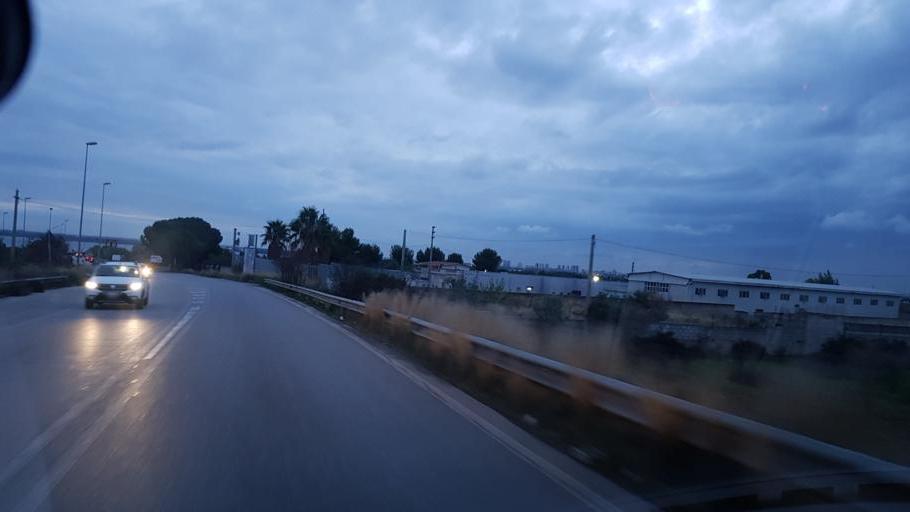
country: IT
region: Apulia
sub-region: Provincia di Taranto
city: Paolo VI
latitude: 40.5143
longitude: 17.2885
